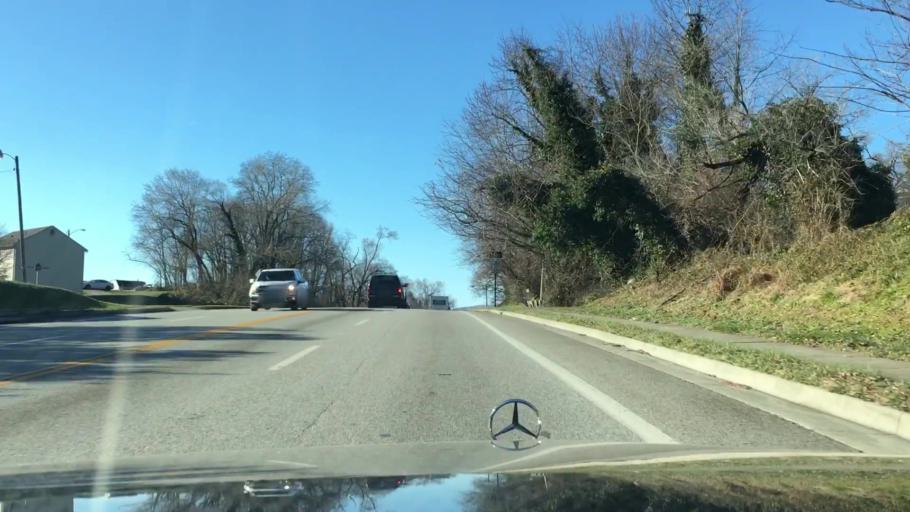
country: US
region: Virginia
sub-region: Roanoke County
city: Vinton
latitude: 37.2869
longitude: -79.9035
